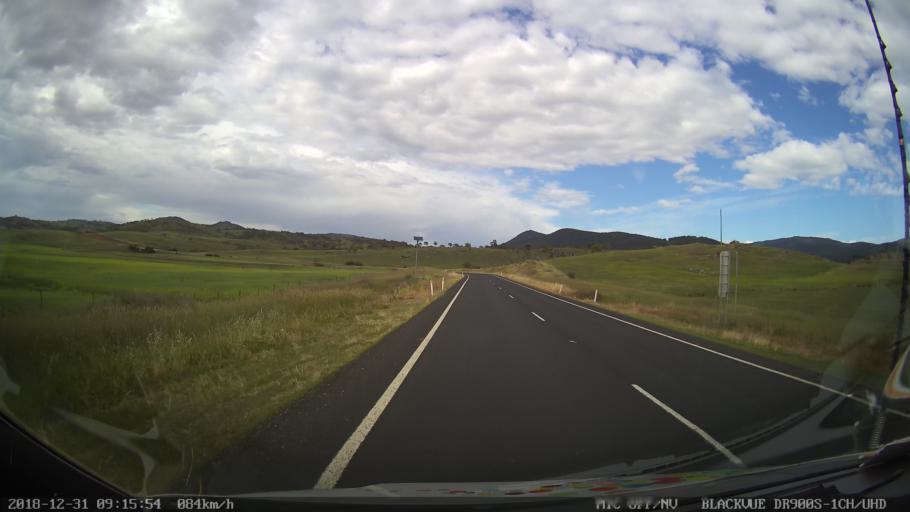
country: AU
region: New South Wales
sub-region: Snowy River
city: Jindabyne
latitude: -36.3904
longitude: 148.5966
